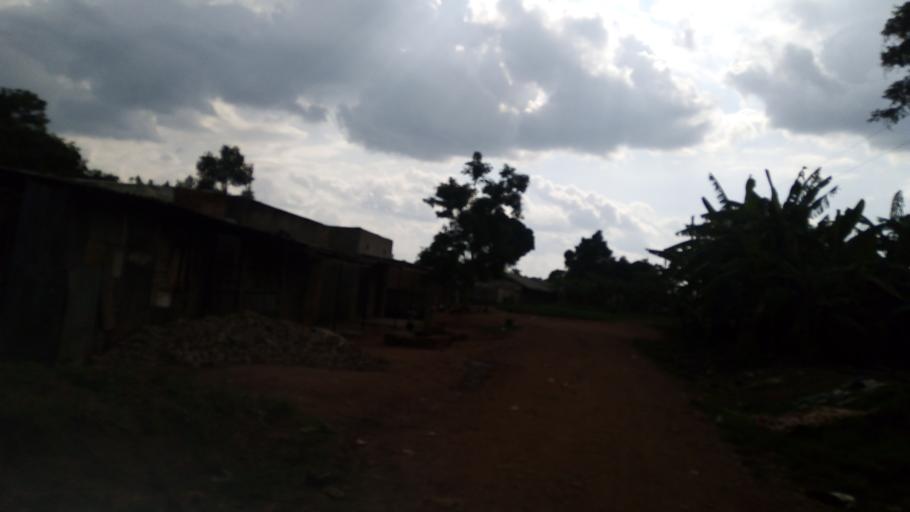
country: UG
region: Eastern Region
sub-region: Mbale District
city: Mbale
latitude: 1.0764
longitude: 34.1543
